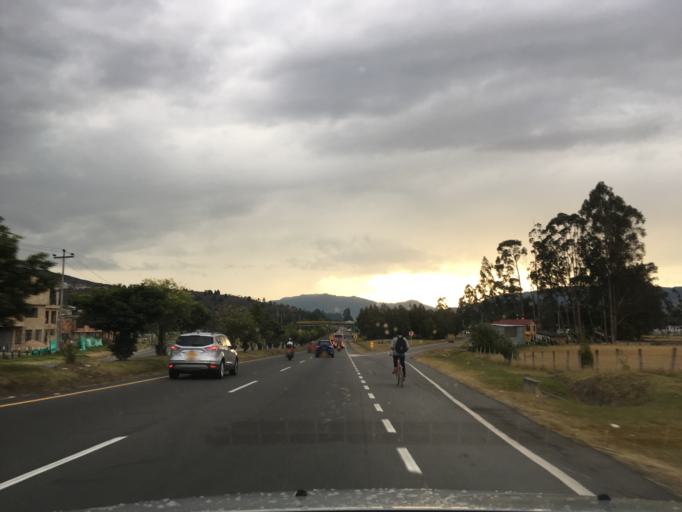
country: CO
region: Cundinamarca
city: Sesquile
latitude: 5.0563
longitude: -73.7943
